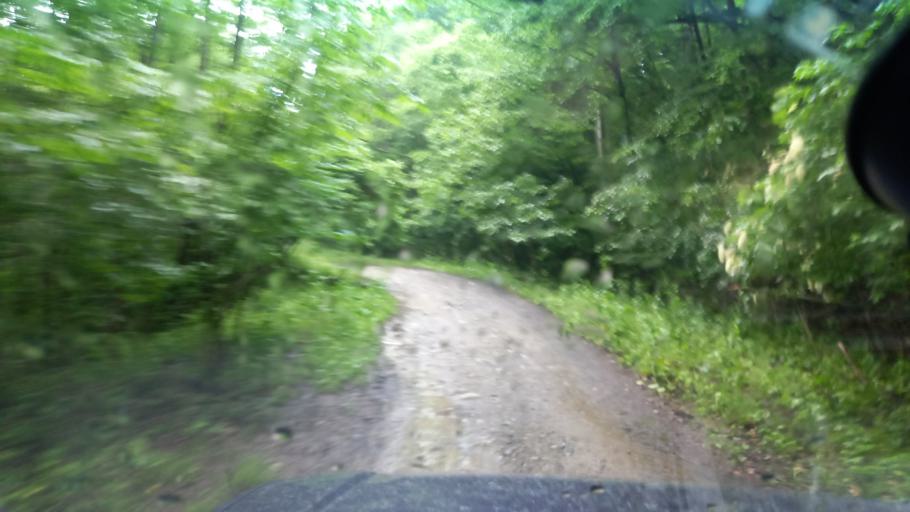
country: RU
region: Krasnodarskiy
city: Psebay
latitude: 44.0177
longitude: 40.7075
